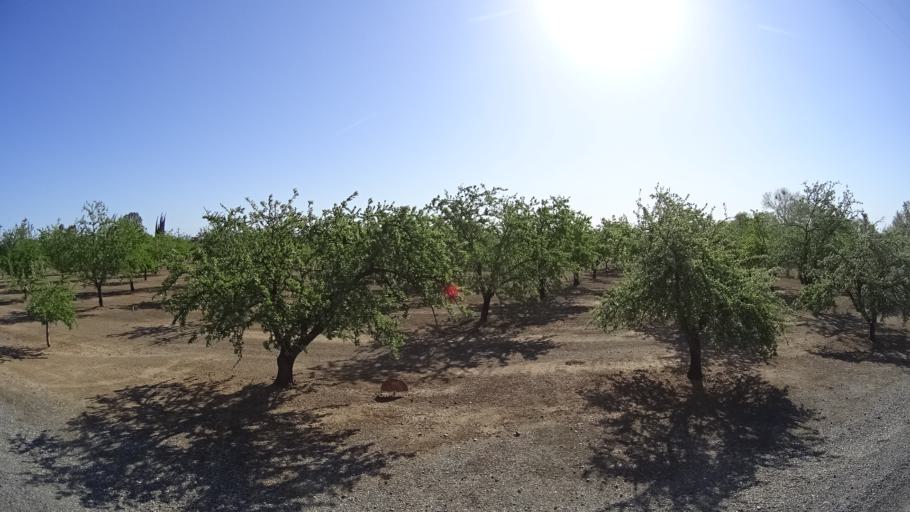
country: US
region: California
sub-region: Glenn County
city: Hamilton City
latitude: 39.7883
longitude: -122.0665
